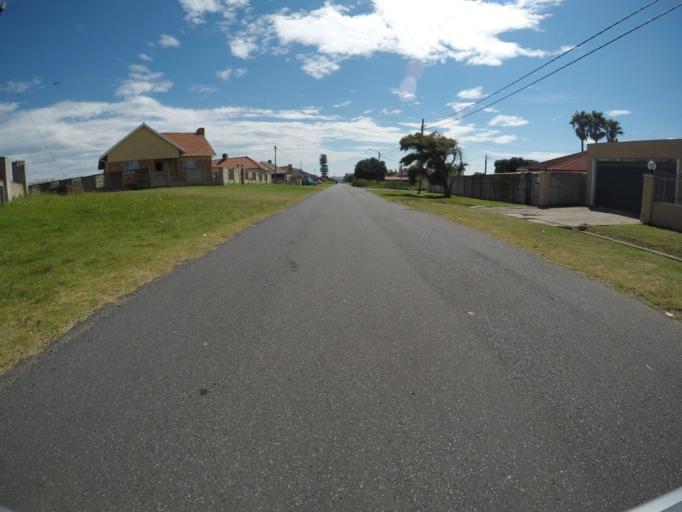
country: ZA
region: Eastern Cape
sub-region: Buffalo City Metropolitan Municipality
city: East London
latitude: -33.0369
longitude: 27.9028
